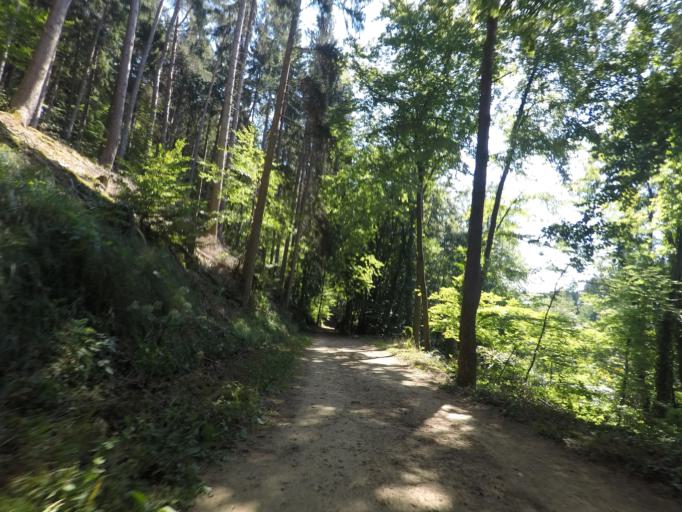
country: LU
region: Luxembourg
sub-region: Canton de Luxembourg
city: Bertrange
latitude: 49.6330
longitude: 6.0469
